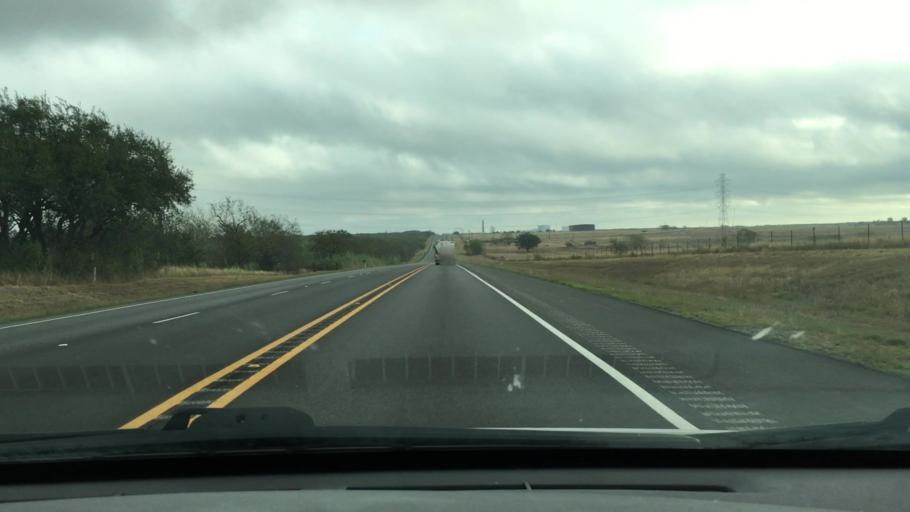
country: US
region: Texas
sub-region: Gonzales County
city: Nixon
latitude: 29.2570
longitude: -97.8100
